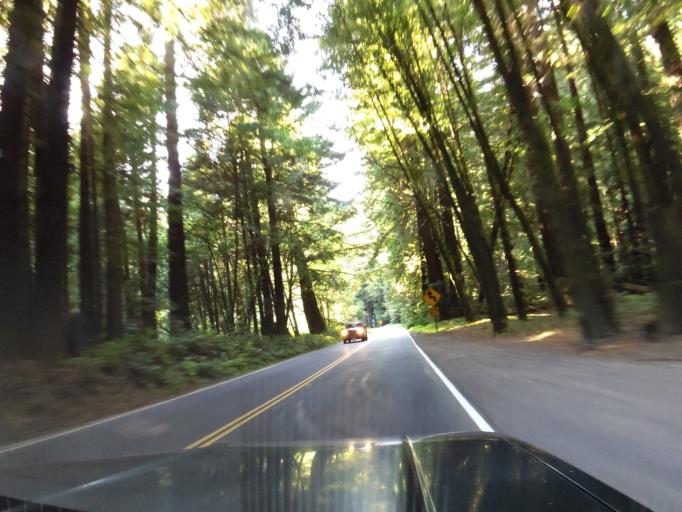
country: US
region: California
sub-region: Mendocino County
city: Boonville
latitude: 39.1551
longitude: -123.6167
